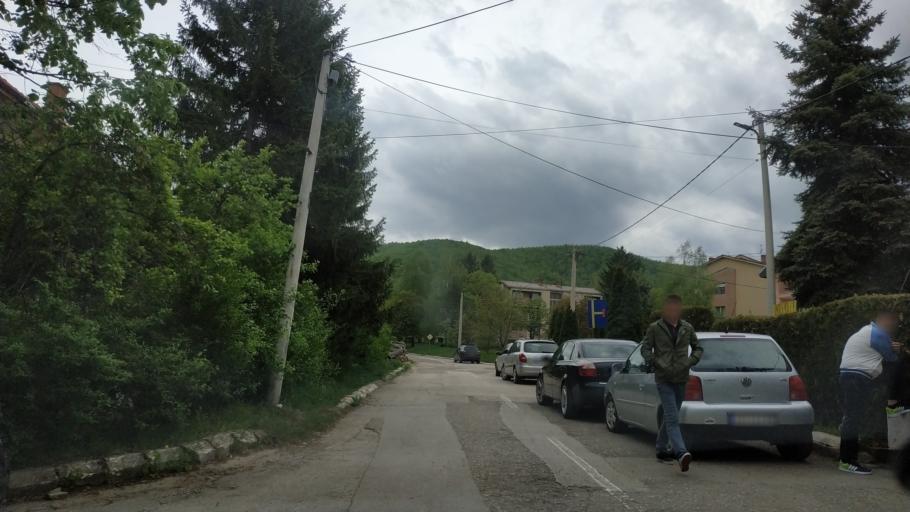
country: RS
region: Central Serbia
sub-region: Zajecarski Okrug
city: Soko Banja
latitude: 43.6419
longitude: 21.8653
